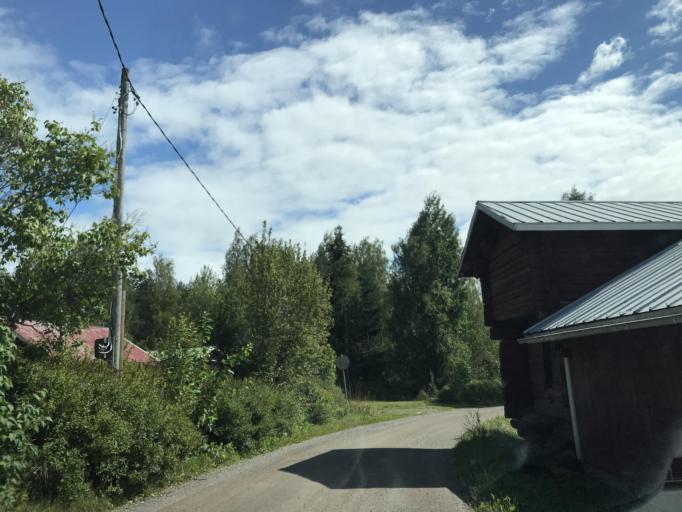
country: FI
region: Uusimaa
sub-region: Helsinki
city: Kaerkoelae
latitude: 60.6284
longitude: 23.8458
